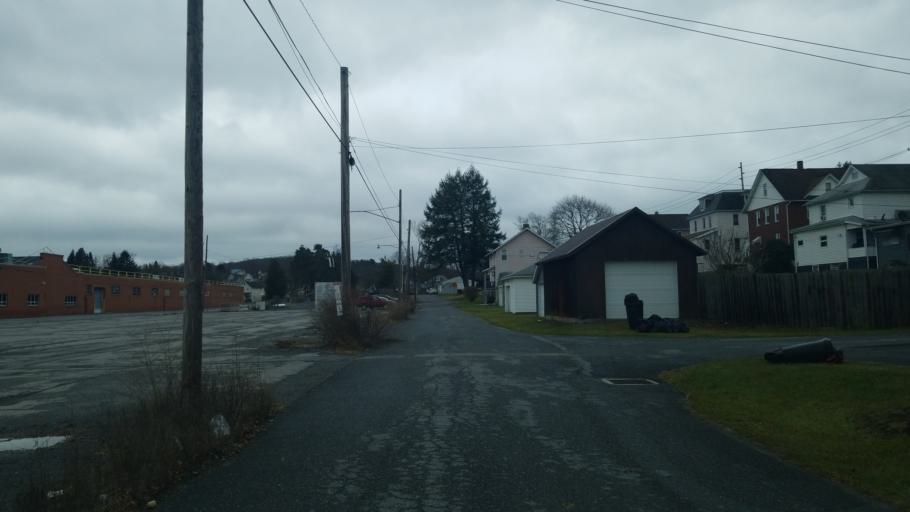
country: US
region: Pennsylvania
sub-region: Clearfield County
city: Sandy
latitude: 41.1146
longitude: -78.7701
